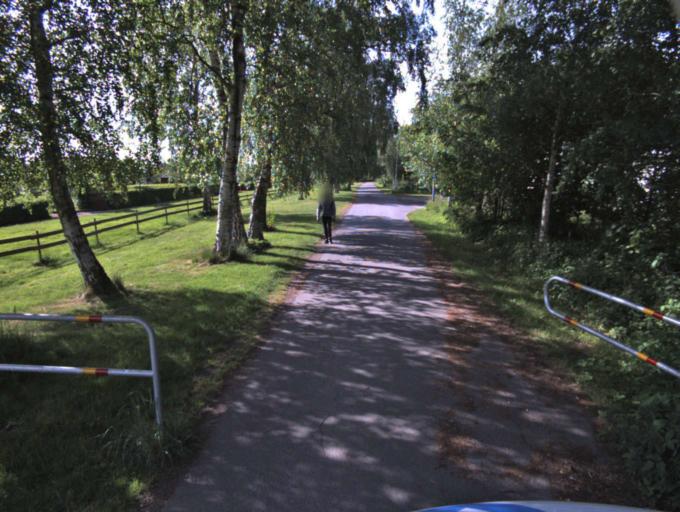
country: SE
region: Skane
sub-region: Kristianstads Kommun
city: Kristianstad
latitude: 56.0340
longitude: 14.1764
